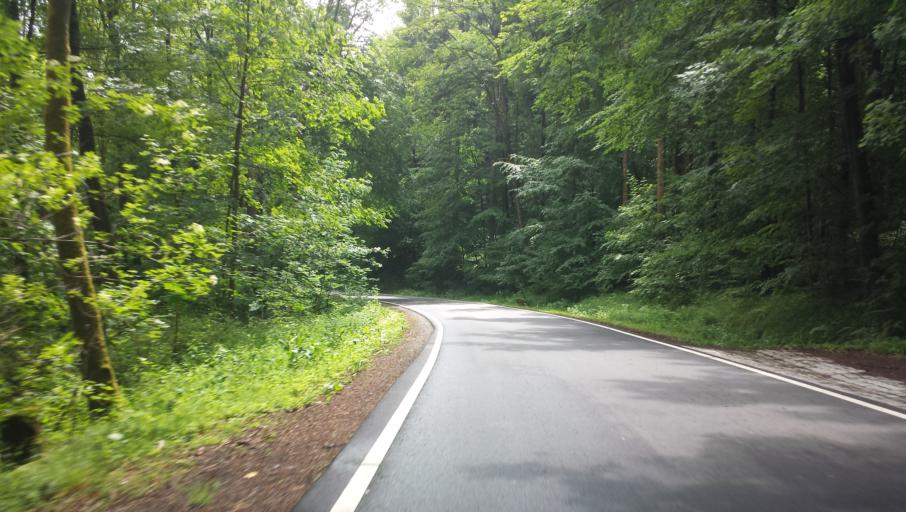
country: DE
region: Hesse
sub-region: Regierungsbezirk Darmstadt
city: Lindenfels
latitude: 49.6894
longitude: 8.7326
